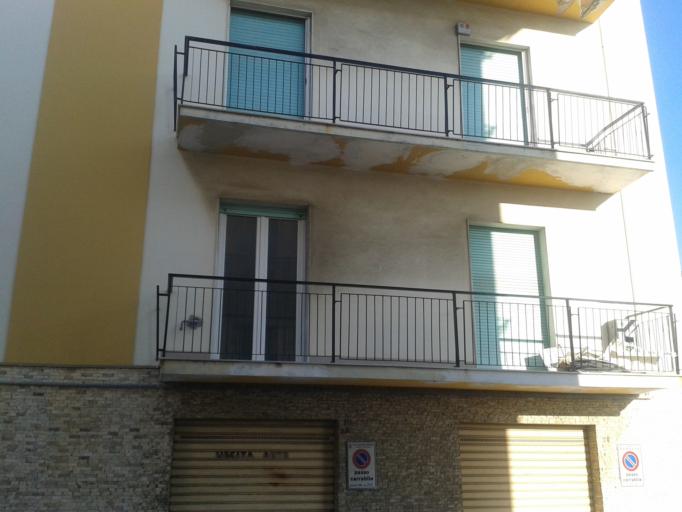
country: IT
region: Liguria
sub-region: Provincia di Savona
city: Albisola Superiore
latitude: 44.3360
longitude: 8.5118
